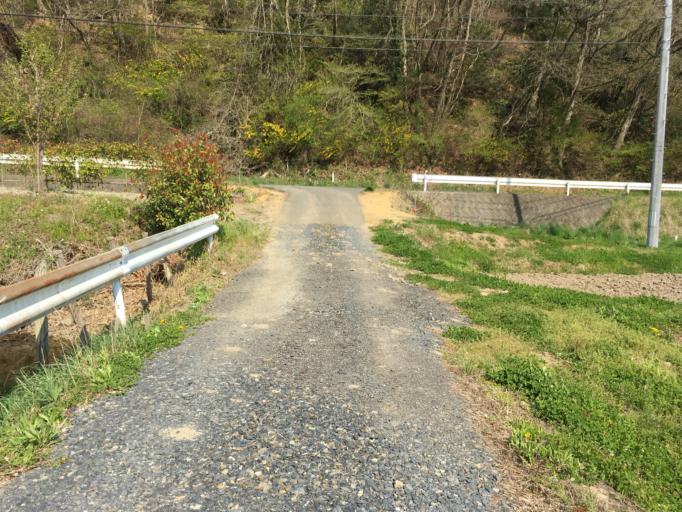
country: JP
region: Iwate
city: Ichinoseki
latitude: 38.8239
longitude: 141.2543
